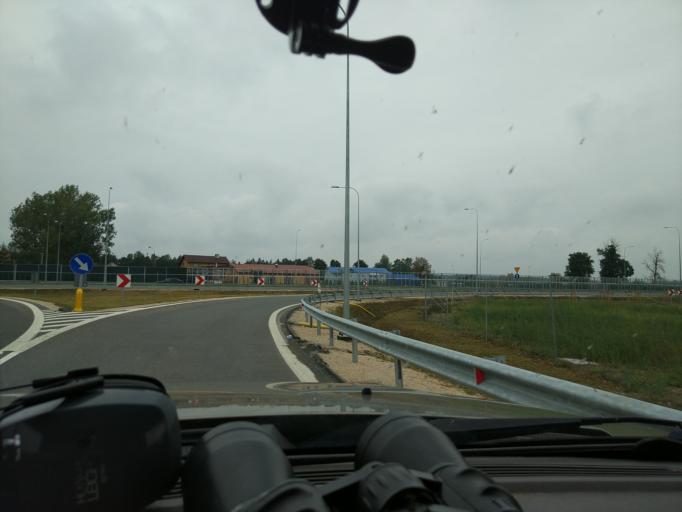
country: PL
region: Podlasie
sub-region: Powiat zambrowski
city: Szumowo
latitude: 52.9111
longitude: 22.1019
